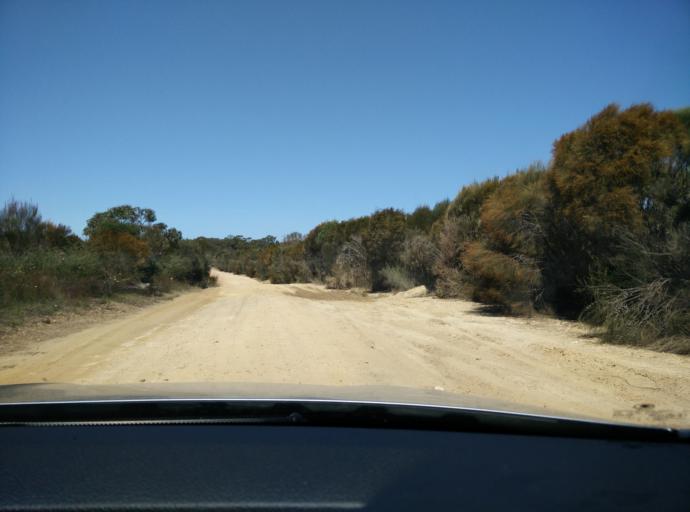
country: AU
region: New South Wales
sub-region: Gosford Shire
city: Umina
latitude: -33.5476
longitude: 151.2865
